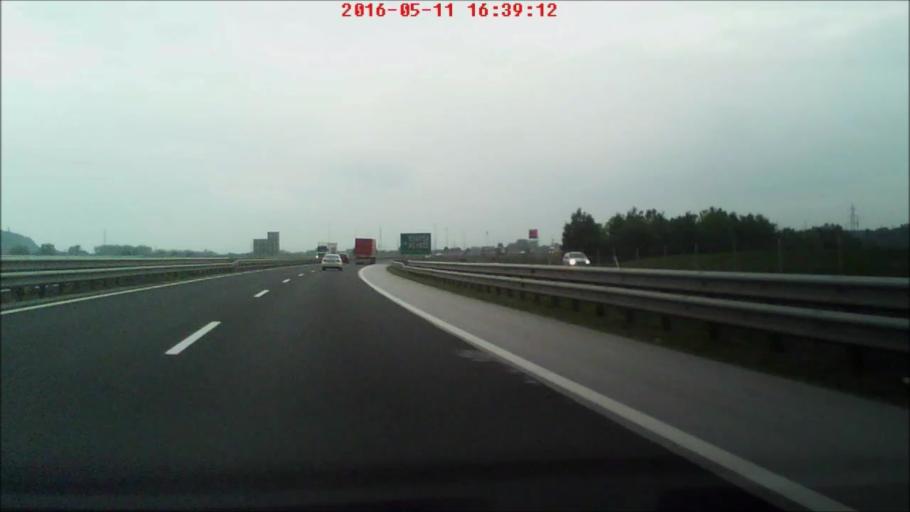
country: SI
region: Miklavz na Dravskem Polju
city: Miklavz na Dravskem Polju
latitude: 46.5400
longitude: 15.6987
